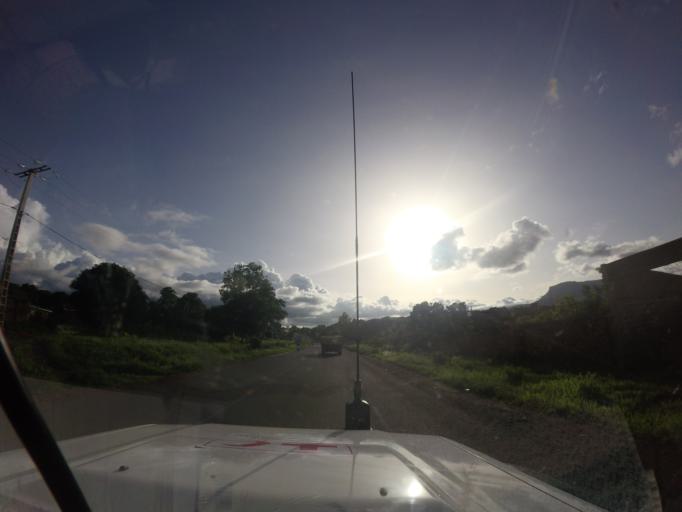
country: GN
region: Kindia
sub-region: Kindia
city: Kindia
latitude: 10.0326
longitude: -12.8605
